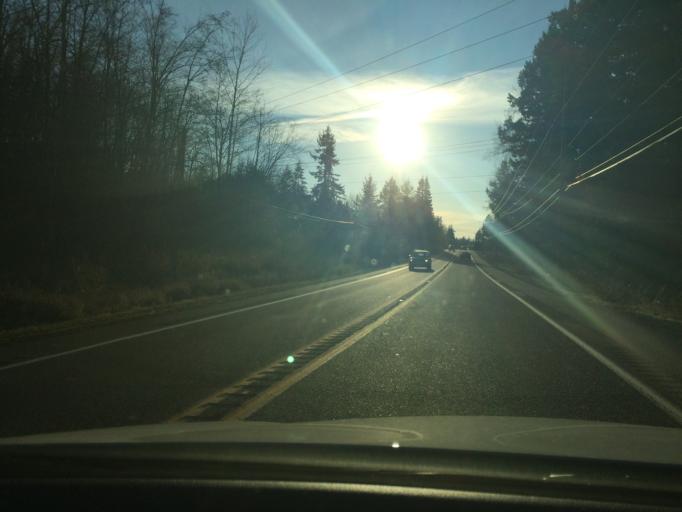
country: US
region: Washington
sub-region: Whatcom County
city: Geneva
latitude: 48.7982
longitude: -122.4094
